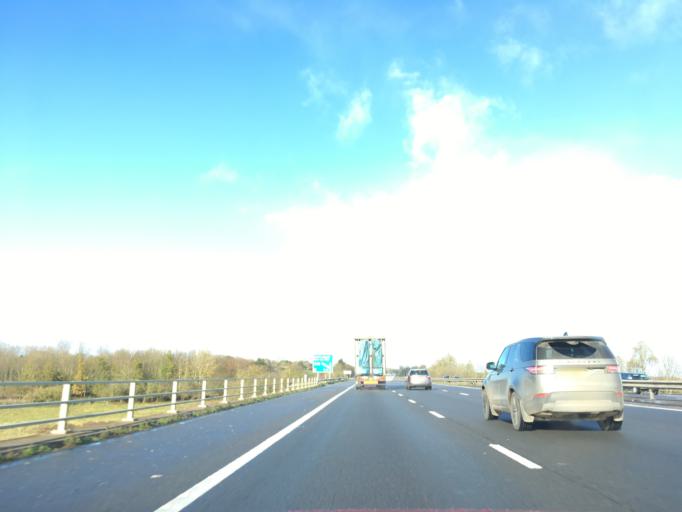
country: GB
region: England
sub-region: Worcestershire
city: Bredon
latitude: 52.0337
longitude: -2.1274
